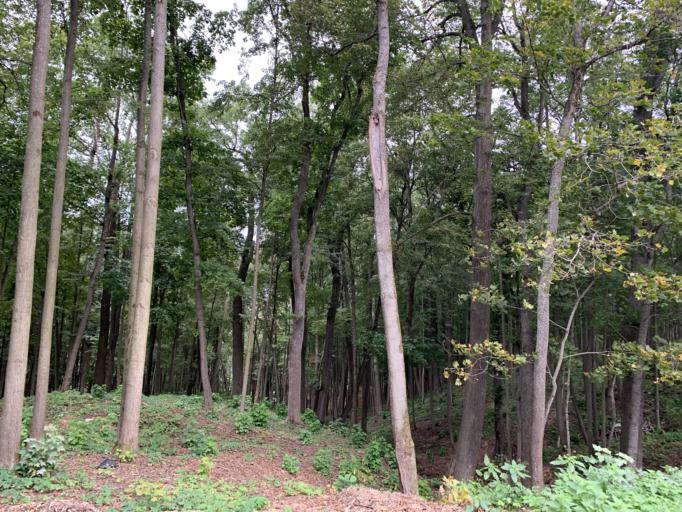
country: RU
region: Moskovskaya
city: Zvenigorod
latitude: 55.7313
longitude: 36.8134
